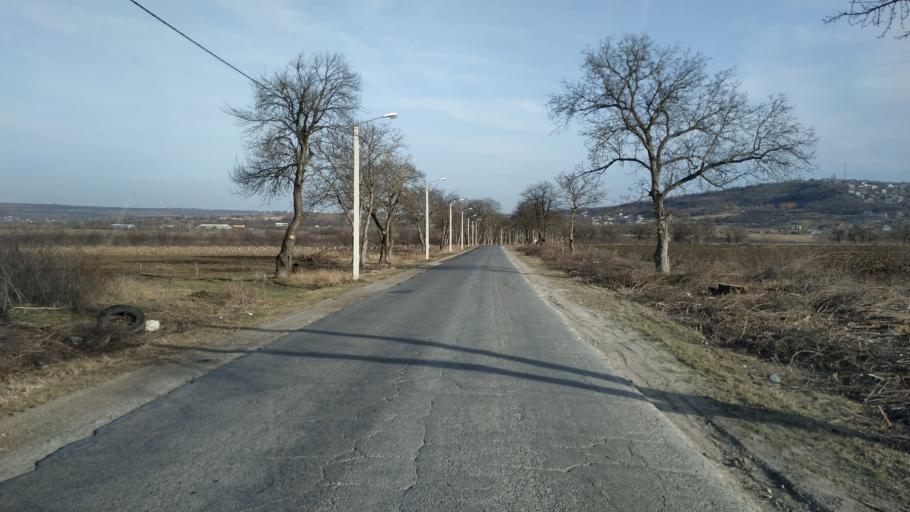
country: MD
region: Chisinau
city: Vatra
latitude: 47.0675
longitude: 28.7279
